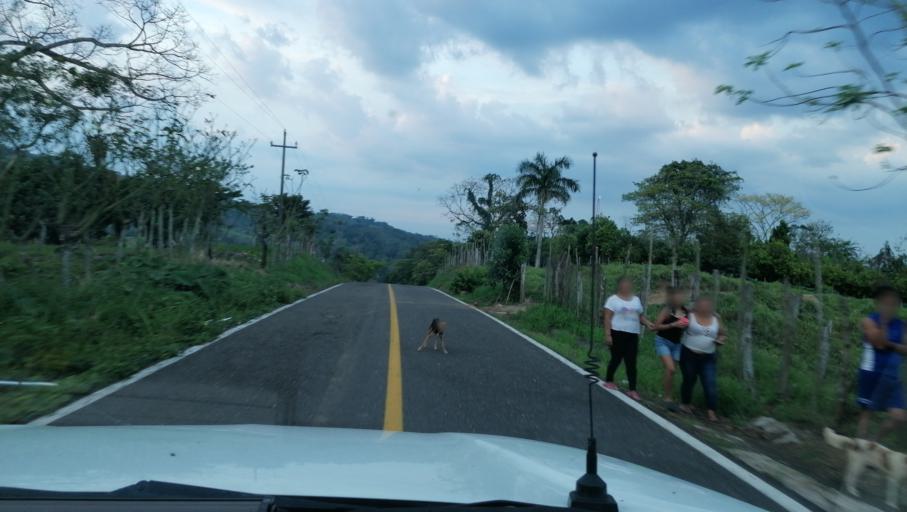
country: MX
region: Chiapas
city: Pichucalco
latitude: 17.5252
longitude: -93.1539
